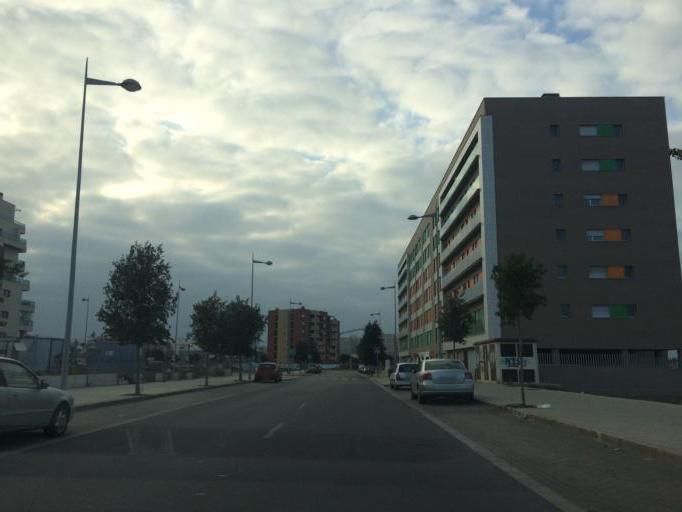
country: ES
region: Andalusia
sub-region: Provincia de Almeria
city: Almeria
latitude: 36.8289
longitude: -2.4424
